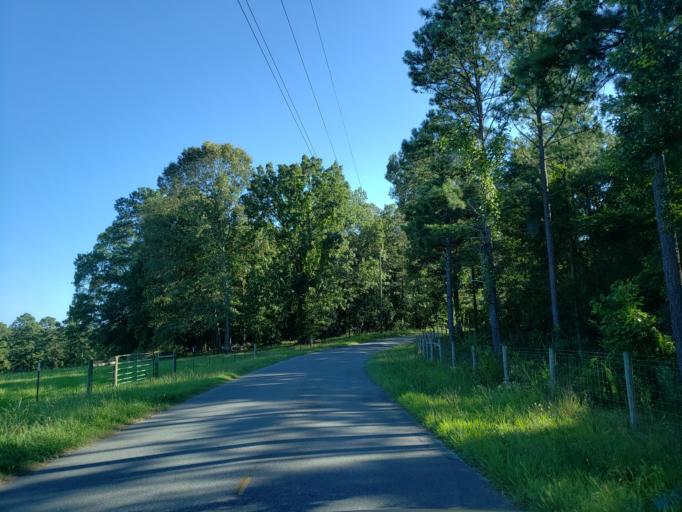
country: US
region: Georgia
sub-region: Polk County
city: Aragon
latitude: 34.1194
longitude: -85.0419
